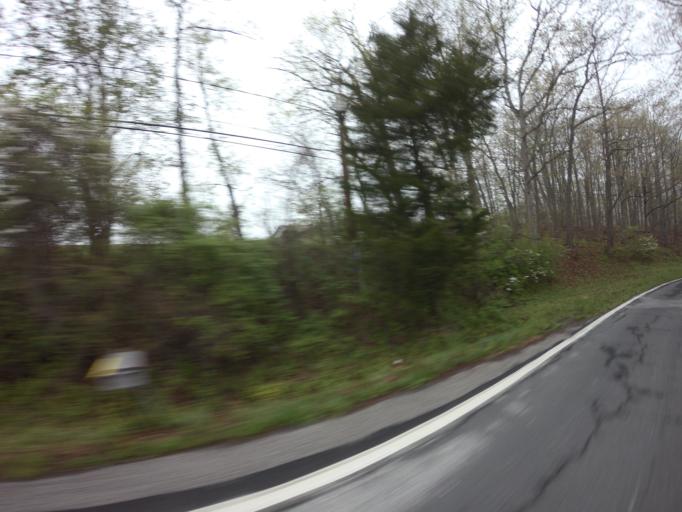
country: US
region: Maryland
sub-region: Carroll County
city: Westminster
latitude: 39.4858
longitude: -76.9874
